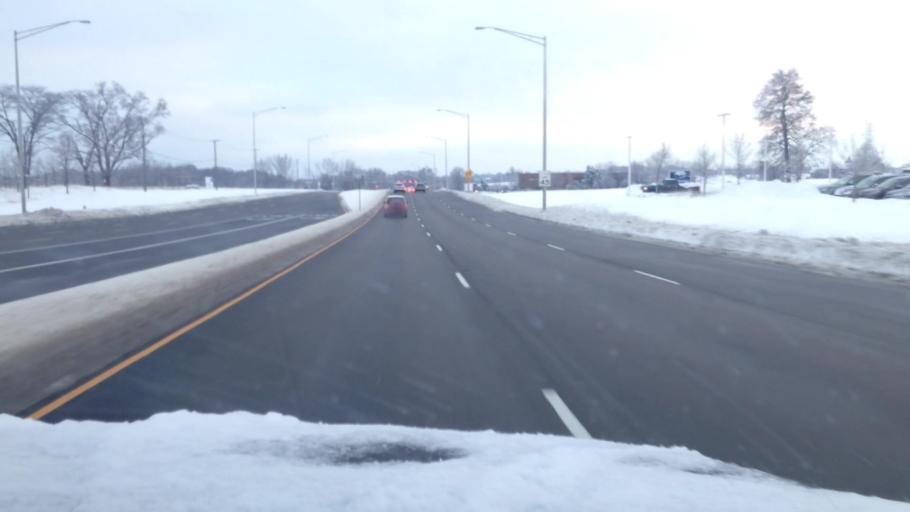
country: US
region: Illinois
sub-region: Kane County
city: Sleepy Hollow
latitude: 42.0705
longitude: -88.3356
